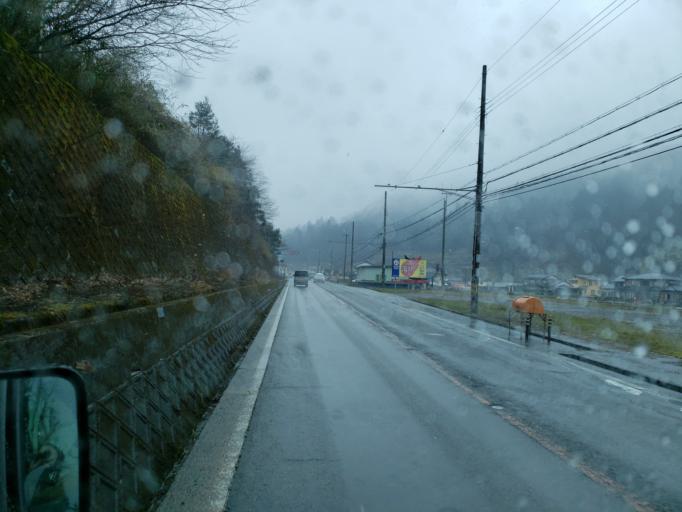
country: JP
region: Hyogo
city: Toyooka
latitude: 35.3834
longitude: 134.6759
